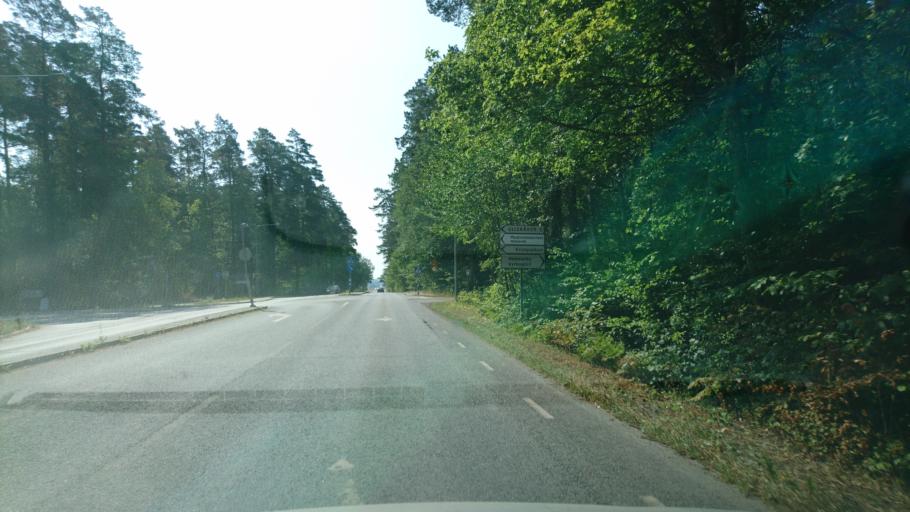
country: SE
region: Uppsala
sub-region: Uppsala Kommun
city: Uppsala
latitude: 59.8284
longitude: 17.6441
